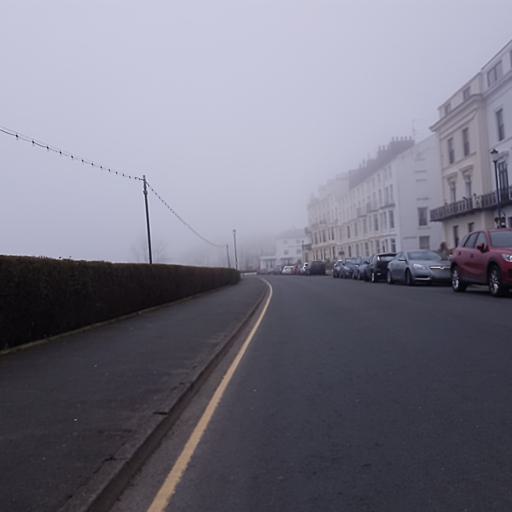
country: GB
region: England
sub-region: North Yorkshire
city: Filey
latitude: 54.2058
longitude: -0.2865
